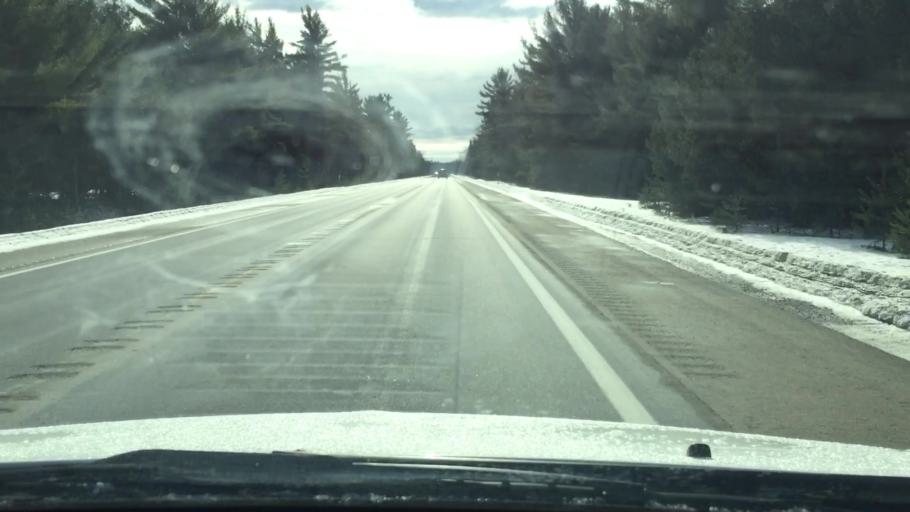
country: US
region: Michigan
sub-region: Kalkaska County
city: Kalkaska
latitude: 44.7138
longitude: -85.1925
